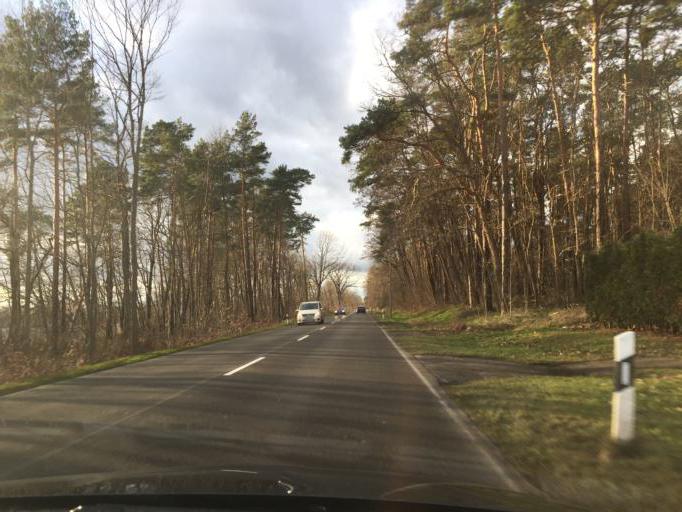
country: DE
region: Brandenburg
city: Kolkwitz
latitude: 51.7503
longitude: 14.2279
